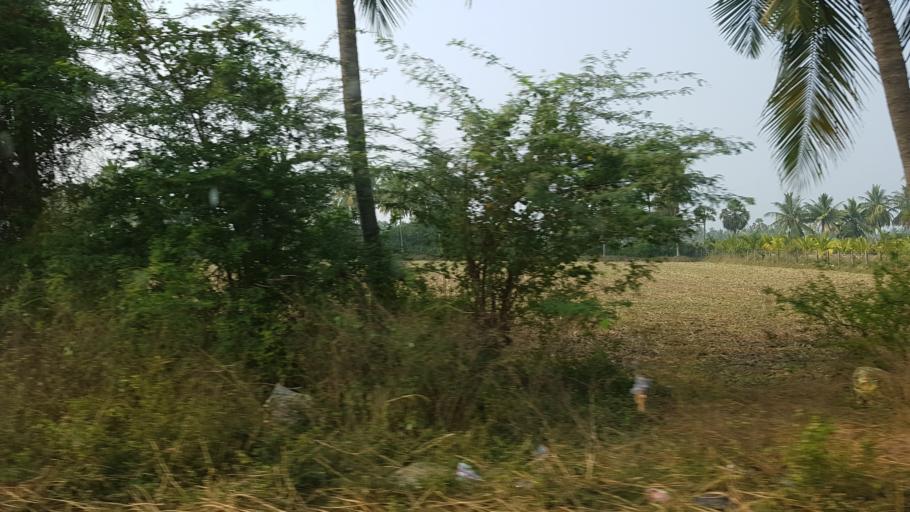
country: IN
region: Andhra Pradesh
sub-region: Krishna
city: Korukollu
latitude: 16.4886
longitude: 81.2473
